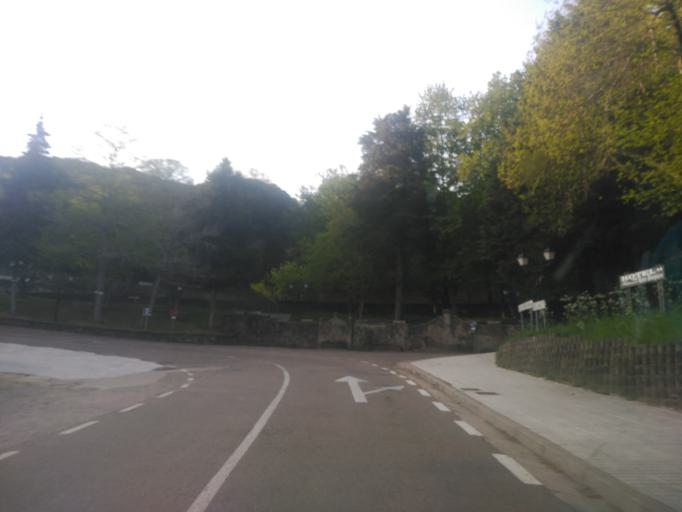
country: ES
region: Castille and Leon
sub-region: Provincia de Salamanca
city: Bejar
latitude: 40.3788
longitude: -5.7631
